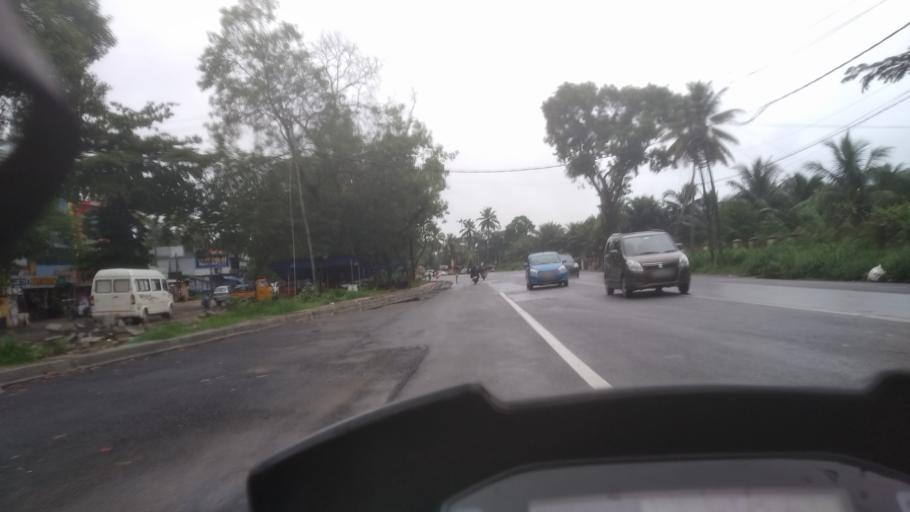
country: IN
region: Kerala
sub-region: Alappuzha
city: Kayankulam
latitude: 9.1491
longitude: 76.5131
